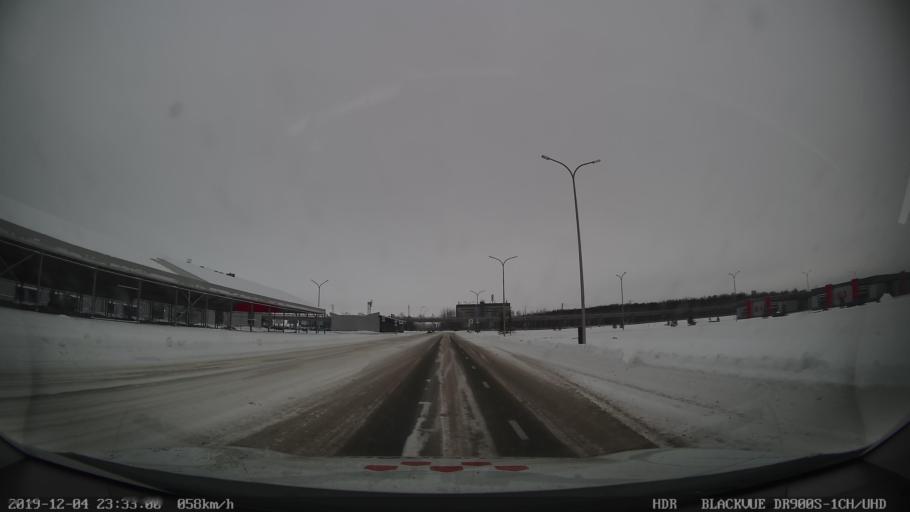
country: RU
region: Tatarstan
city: Stolbishchi
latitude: 55.6137
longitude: 49.2963
